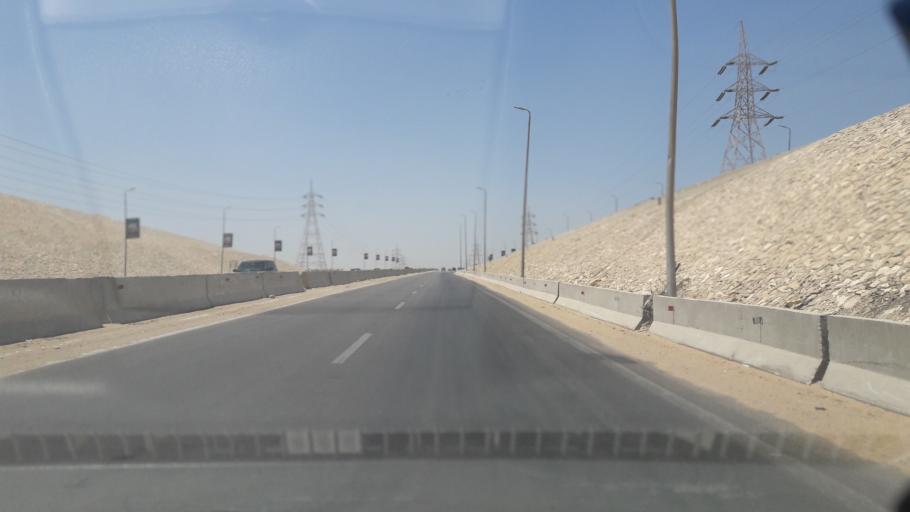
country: EG
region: Al Jizah
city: Al Jizah
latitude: 30.0012
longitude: 31.0901
